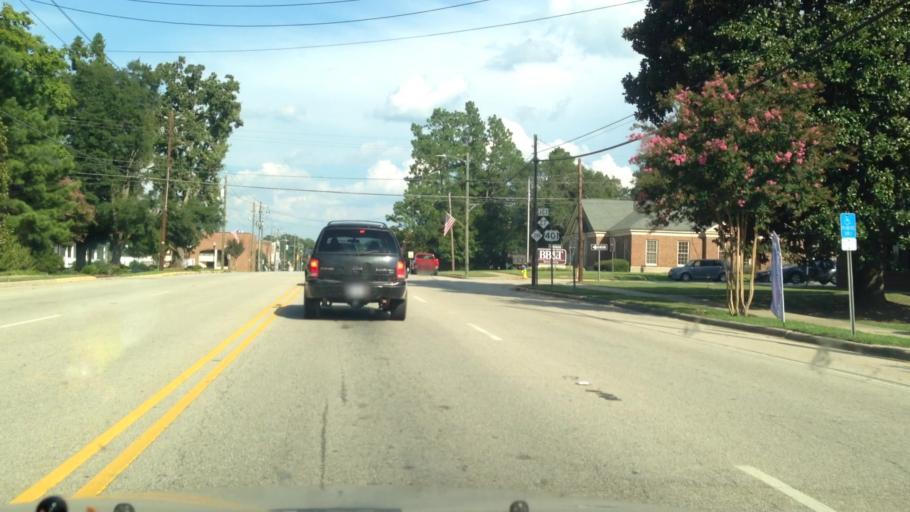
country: US
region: North Carolina
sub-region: Harnett County
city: Lillington
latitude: 35.3996
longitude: -78.8194
